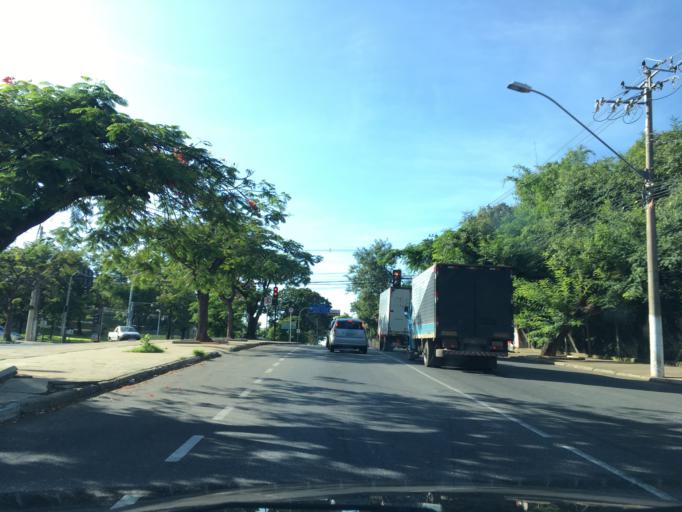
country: BR
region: Minas Gerais
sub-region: Belo Horizonte
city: Belo Horizonte
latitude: -19.8636
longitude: -43.9741
